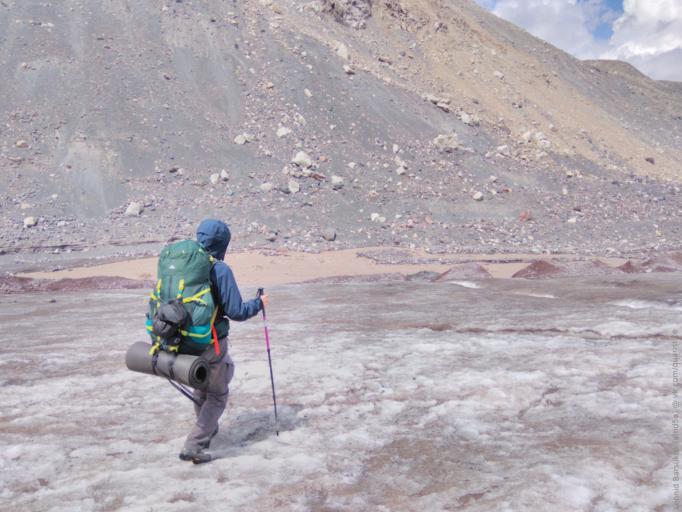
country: RU
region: Kabardino-Balkariya
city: Terskol
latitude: 43.3629
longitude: 42.5390
